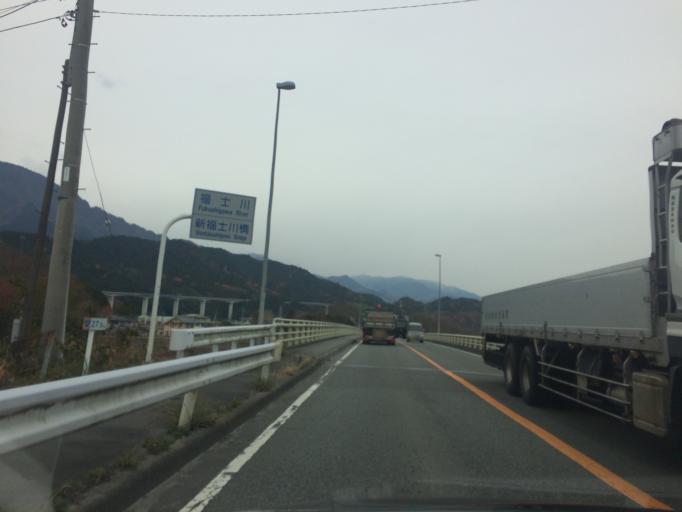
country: JP
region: Shizuoka
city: Fujinomiya
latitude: 35.2399
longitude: 138.4878
